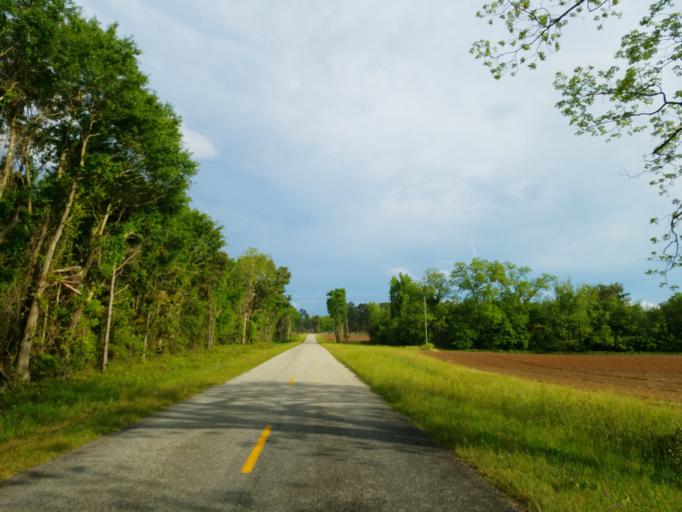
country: US
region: Georgia
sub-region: Dooly County
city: Vienna
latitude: 32.1653
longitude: -83.7638
